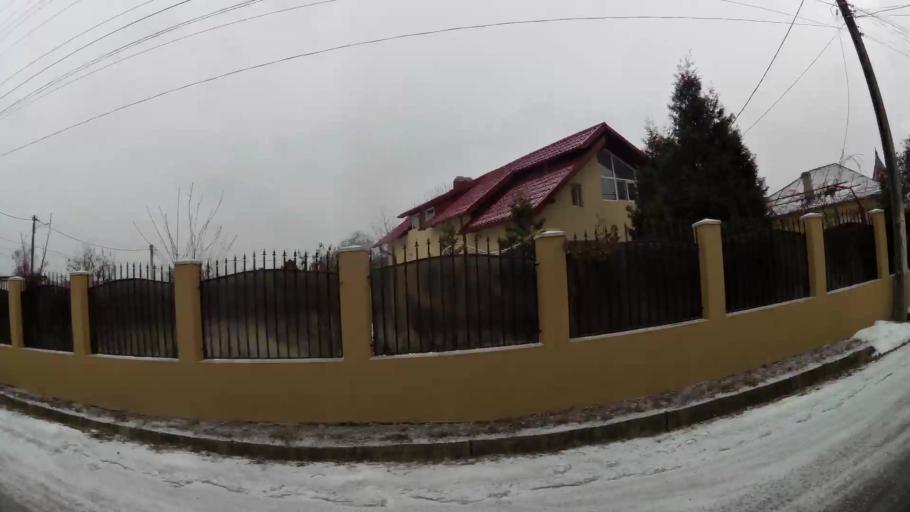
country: RO
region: Dambovita
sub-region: Municipiul Targoviste
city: Targoviste
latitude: 44.9413
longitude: 25.4752
